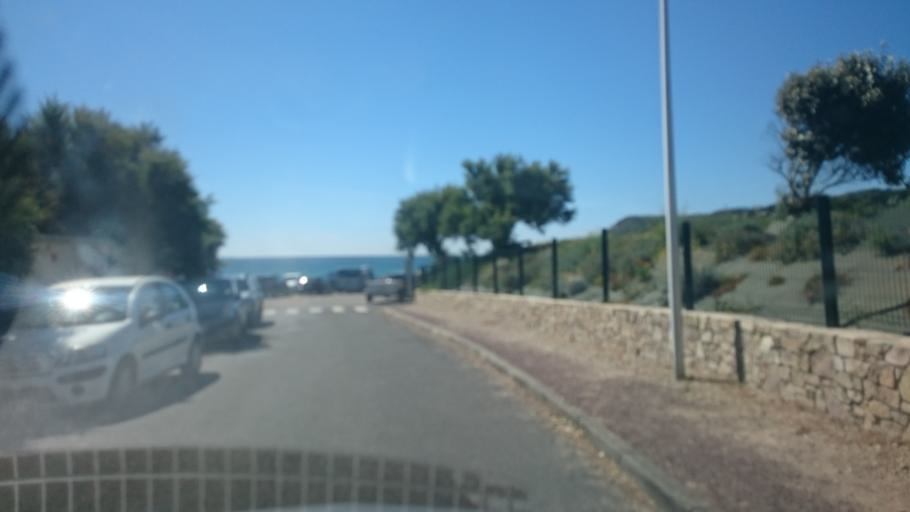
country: FR
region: Lower Normandy
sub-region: Departement de la Manche
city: Flamanville
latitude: 49.5086
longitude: -1.8497
